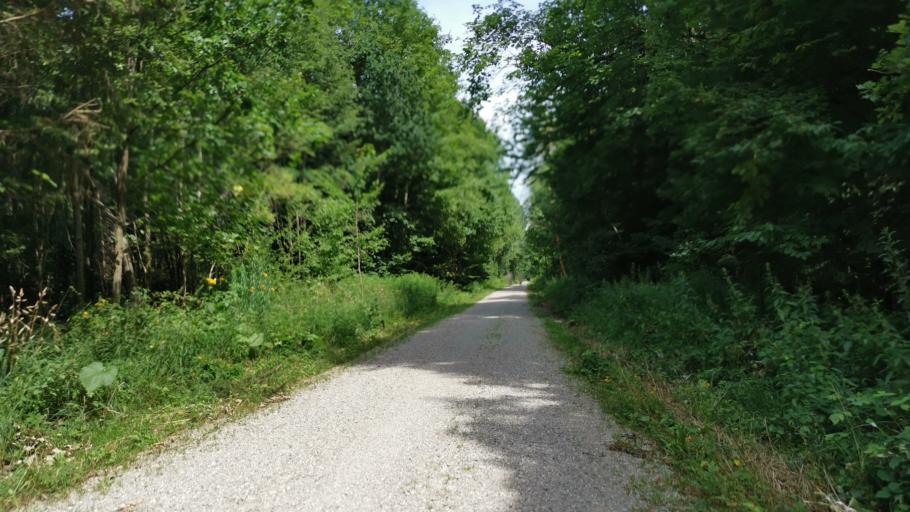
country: DE
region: Bavaria
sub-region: Upper Bavaria
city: Neuried
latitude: 48.0752
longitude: 11.4794
